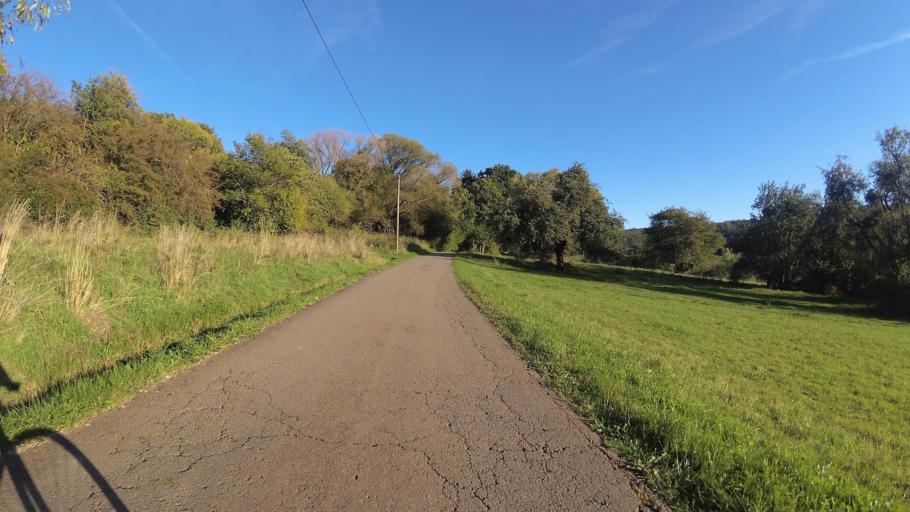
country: DE
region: Saarland
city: Freisen
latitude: 49.5126
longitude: 7.2185
